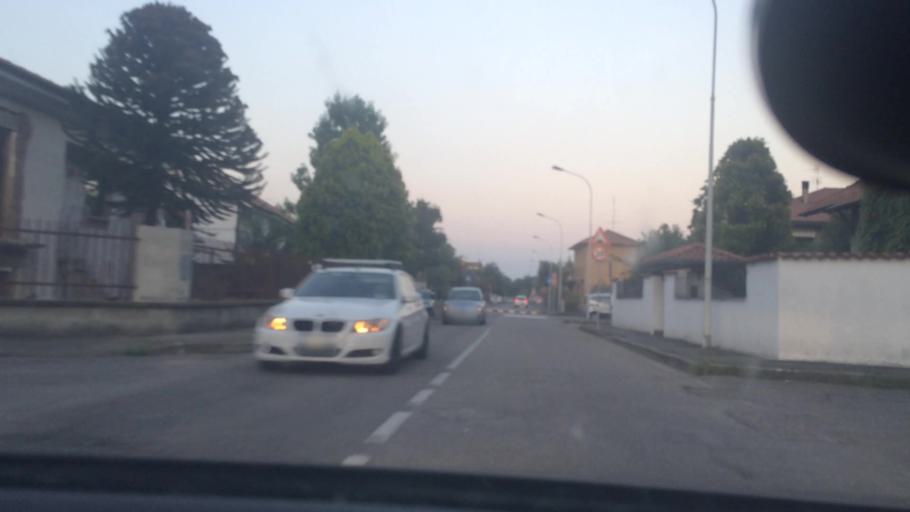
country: IT
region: Lombardy
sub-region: Citta metropolitana di Milano
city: Parabiago
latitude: 45.5458
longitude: 8.9410
